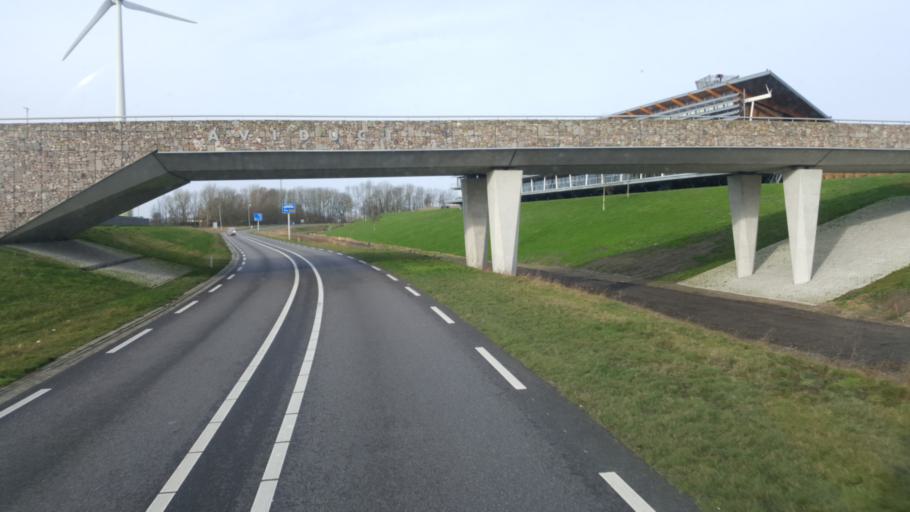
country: NL
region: North Holland
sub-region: Gemeente Zaanstad
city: Zaanstad
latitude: 52.4340
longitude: 4.7317
